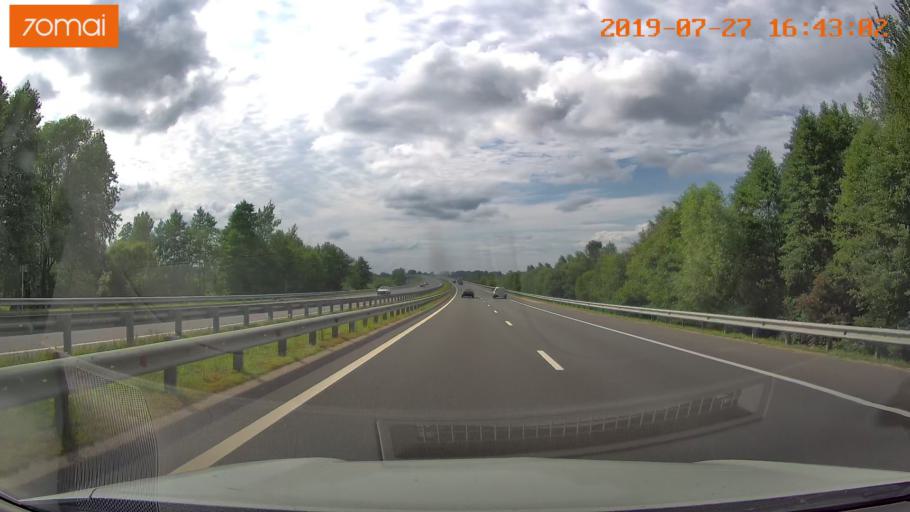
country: RU
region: Kaliningrad
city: Gvardeysk
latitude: 54.6690
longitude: 21.1125
